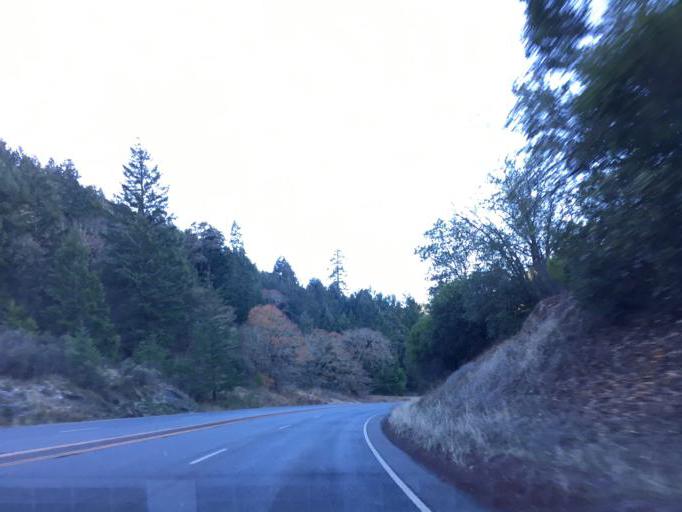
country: US
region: California
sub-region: Mendocino County
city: Laytonville
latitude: 39.8266
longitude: -123.5832
